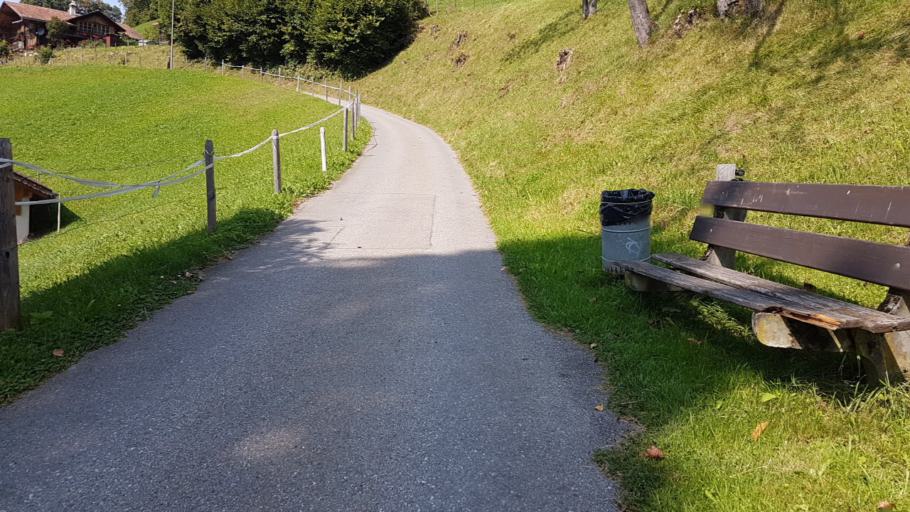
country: CH
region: Bern
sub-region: Frutigen-Niedersimmental District
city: Aeschi
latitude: 46.5905
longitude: 7.7233
